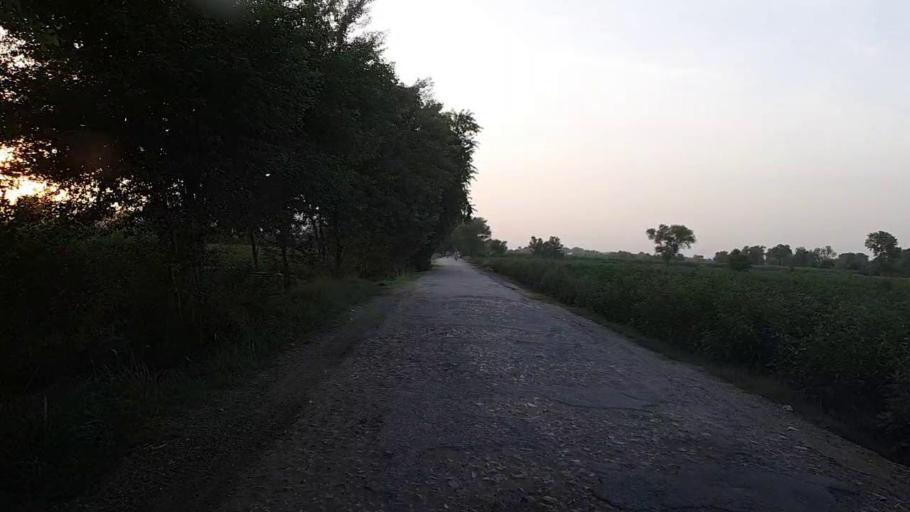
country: PK
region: Sindh
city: Ubauro
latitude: 28.3001
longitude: 69.7970
